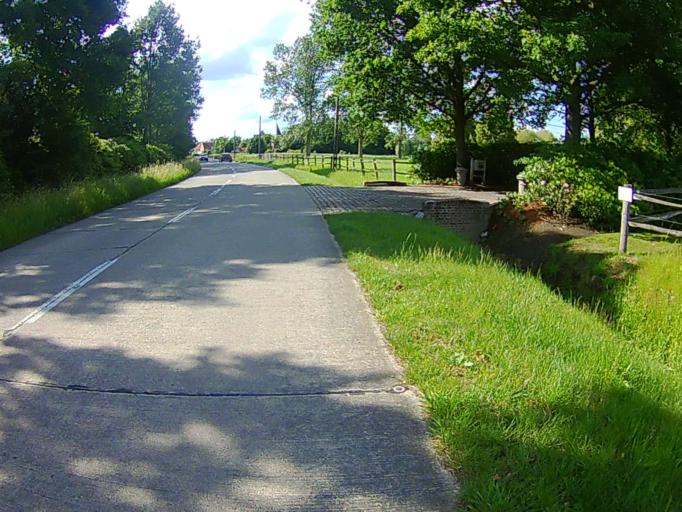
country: BE
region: Flanders
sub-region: Provincie Antwerpen
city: Berlaar
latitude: 51.1255
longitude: 4.6776
